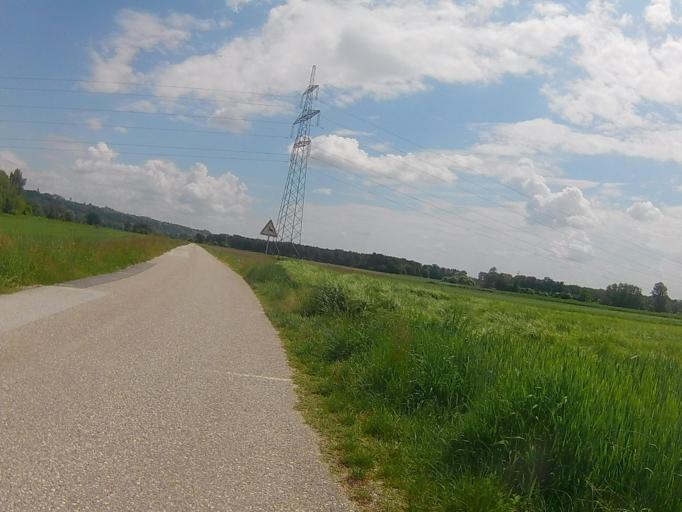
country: SI
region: Starse
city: Starse
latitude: 46.4673
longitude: 15.7749
